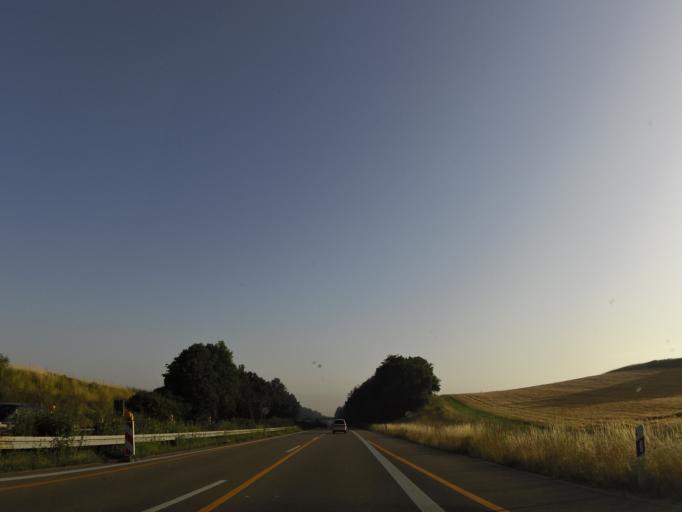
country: DE
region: Bavaria
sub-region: Swabia
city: Holzheim
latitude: 48.3774
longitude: 10.0855
